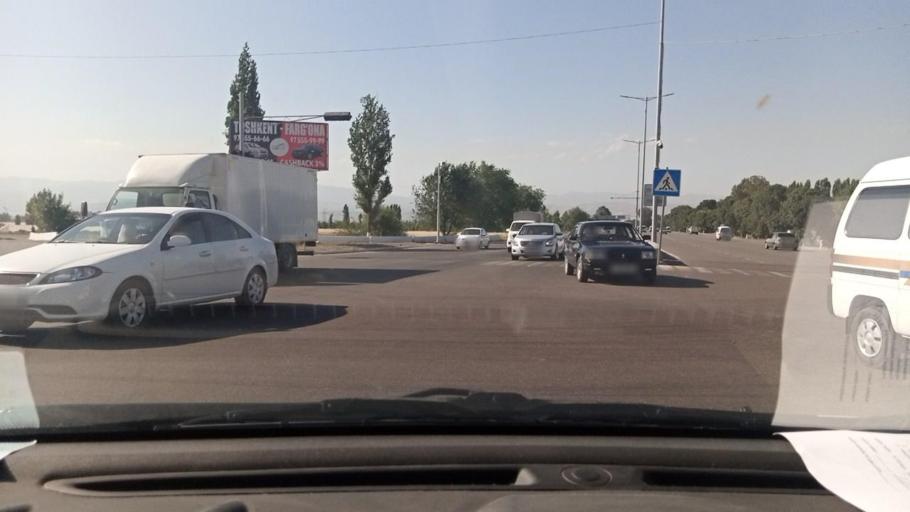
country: UZ
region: Toshkent
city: Ohangaron
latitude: 40.9205
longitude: 69.5973
